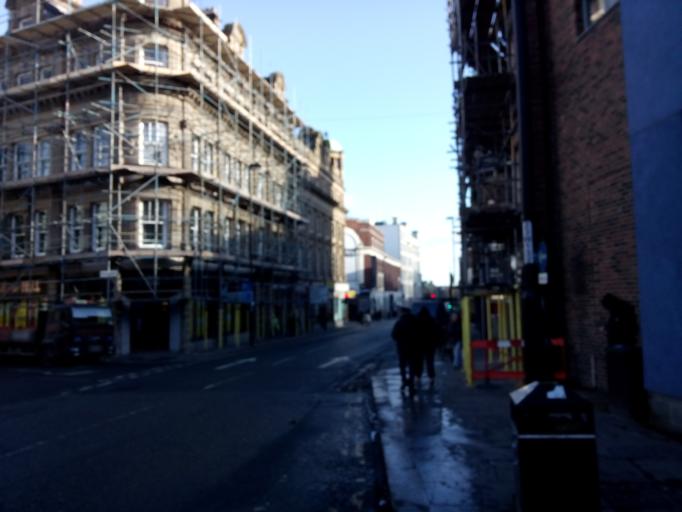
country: GB
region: England
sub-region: Newcastle upon Tyne
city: Newcastle upon Tyne
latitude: 54.9705
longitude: -1.6202
